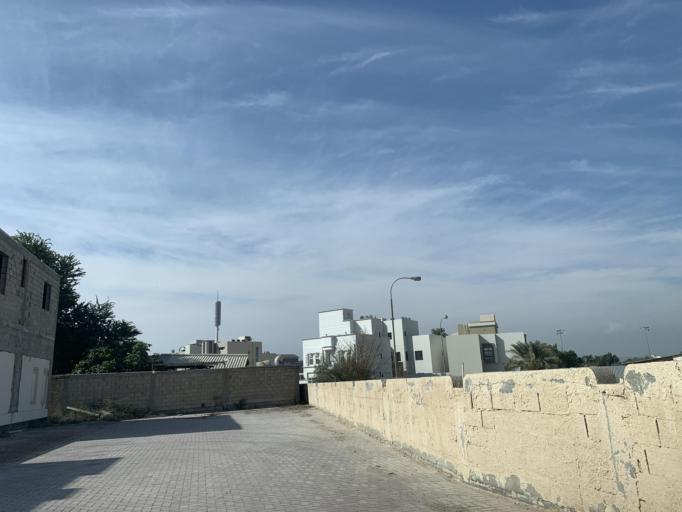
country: BH
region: Central Governorate
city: Madinat Hamad
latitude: 26.1238
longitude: 50.4747
